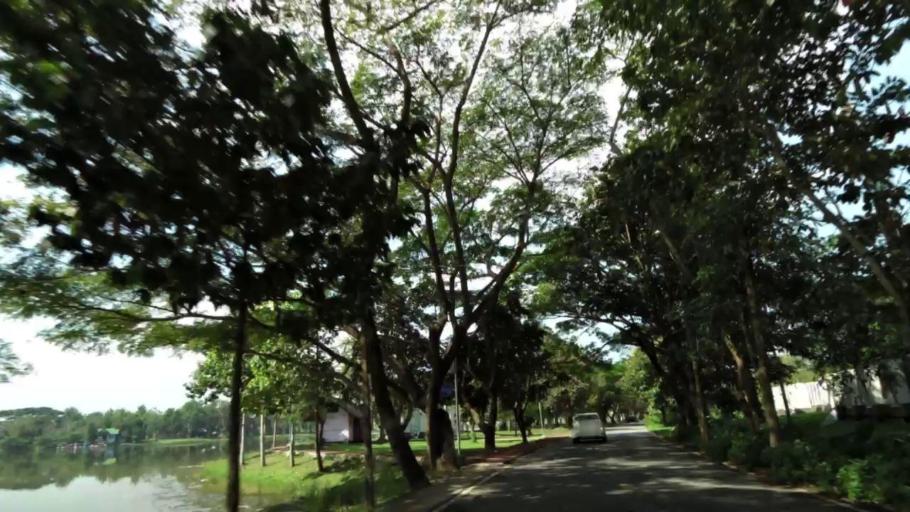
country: TH
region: Chiang Rai
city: Chiang Rai
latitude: 19.8863
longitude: 99.8053
